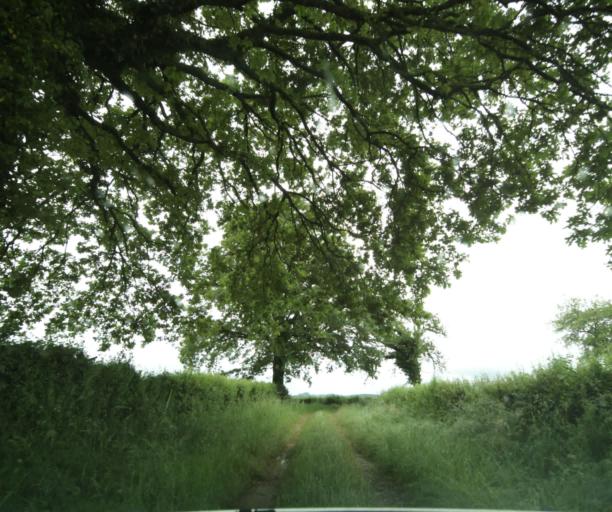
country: FR
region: Bourgogne
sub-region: Departement de Saone-et-Loire
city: Charolles
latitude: 46.4588
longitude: 4.3551
